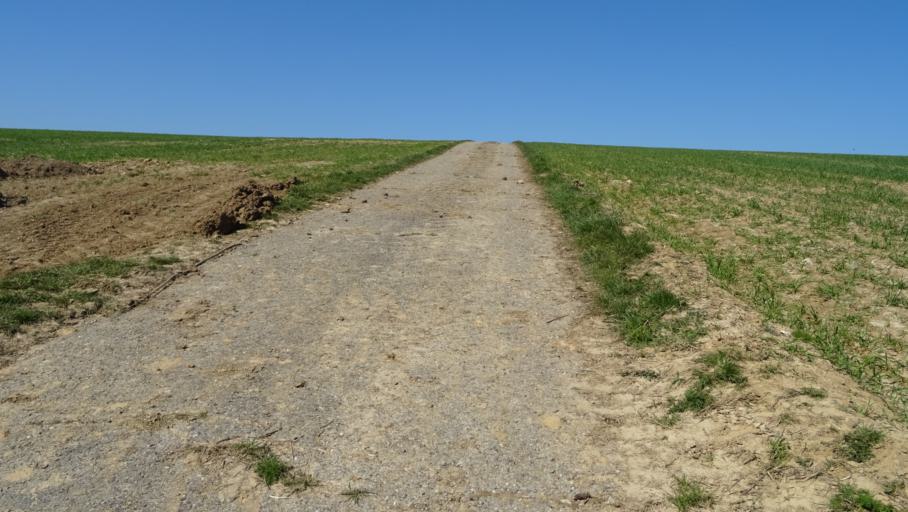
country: DE
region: Baden-Wuerttemberg
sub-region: Karlsruhe Region
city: Limbach
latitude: 49.4152
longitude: 9.2491
